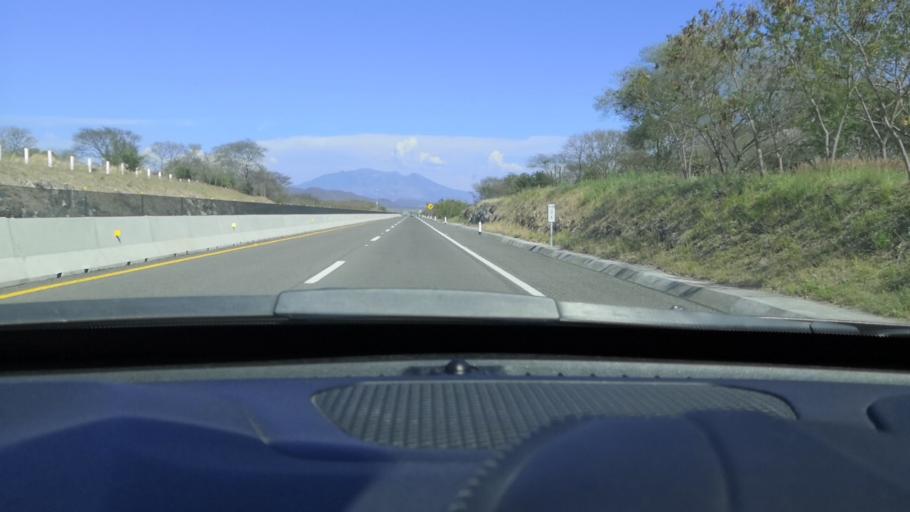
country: MX
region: Nayarit
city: San Pedro Lagunillas
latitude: 21.0970
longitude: -104.7556
